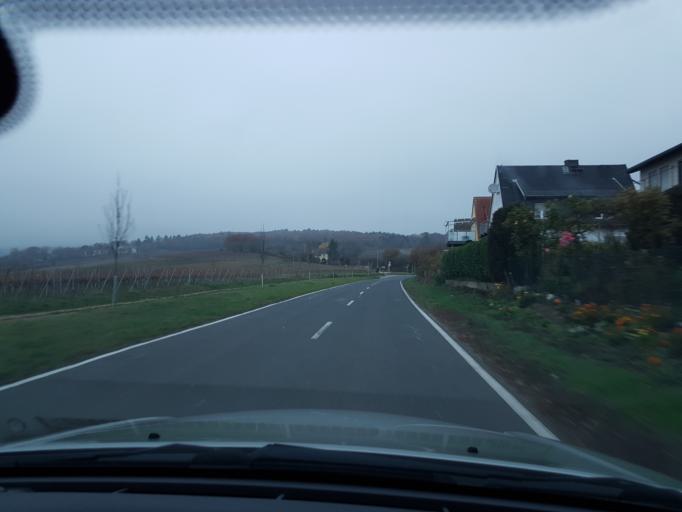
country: DE
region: Hesse
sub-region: Regierungsbezirk Darmstadt
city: Kiedrich
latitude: 50.0366
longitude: 8.0754
